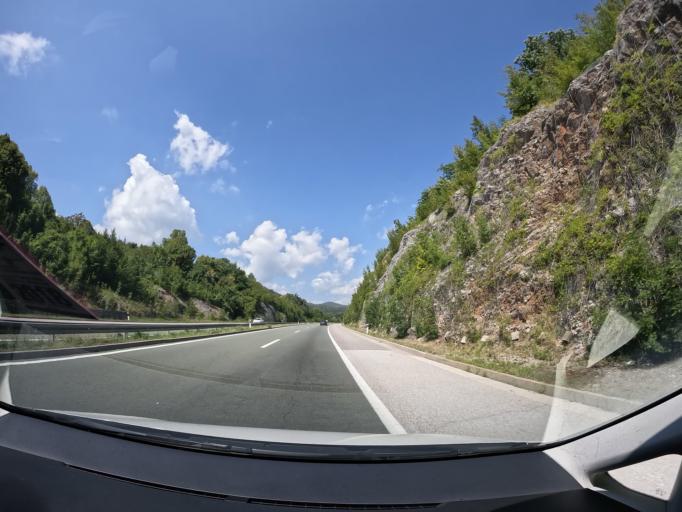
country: HR
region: Primorsko-Goranska
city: Matulji
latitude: 45.3797
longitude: 14.3096
